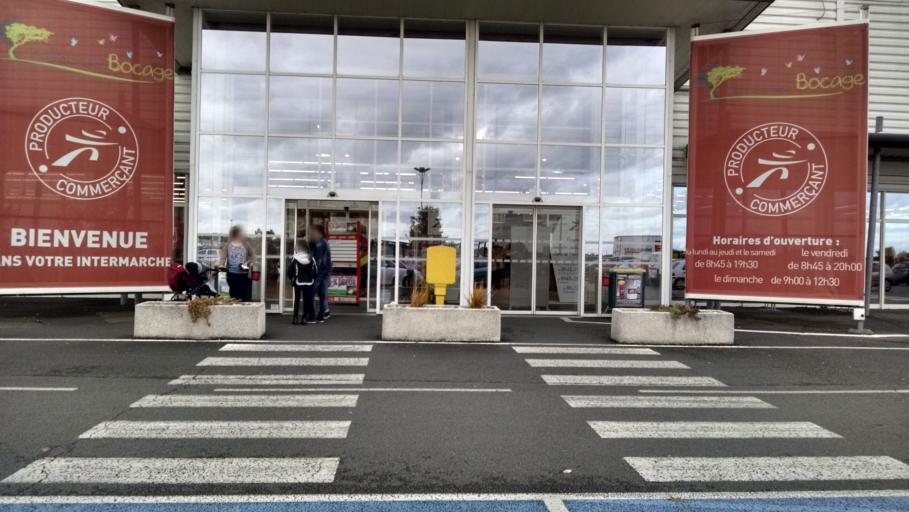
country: FR
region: Pays de la Loire
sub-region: Departement de la Vendee
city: Montaigu
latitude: 46.9808
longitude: -1.2987
